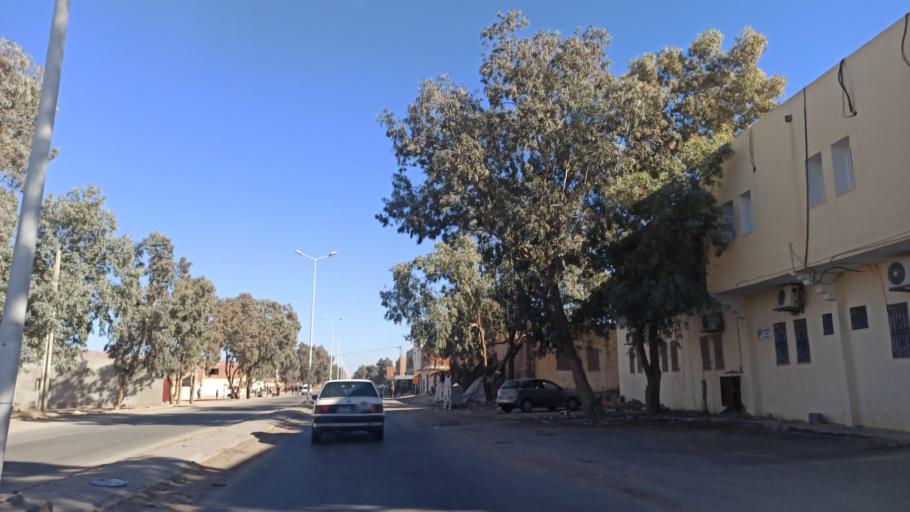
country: TN
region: Gafsa
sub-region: Gafsa Municipality
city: Gafsa
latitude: 34.4010
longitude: 8.7240
